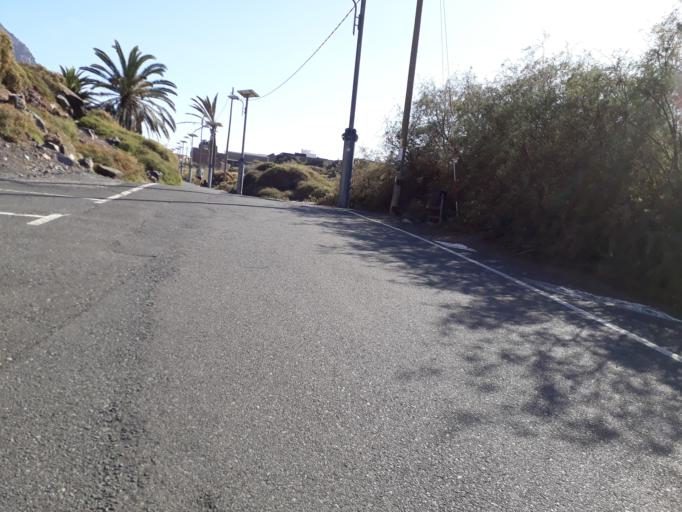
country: ES
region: Canary Islands
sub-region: Provincia de Santa Cruz de Tenerife
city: Alajero
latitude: 28.0985
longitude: -17.3466
